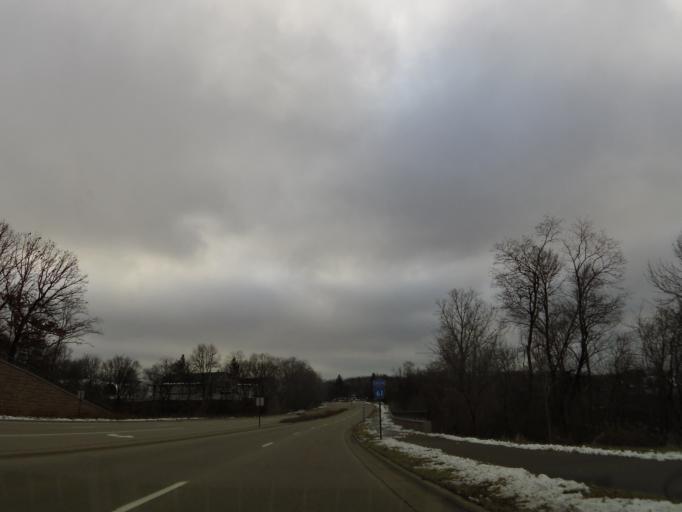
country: US
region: Minnesota
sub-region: Hennepin County
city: Minnetonka Mills
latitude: 44.9054
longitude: -93.4280
